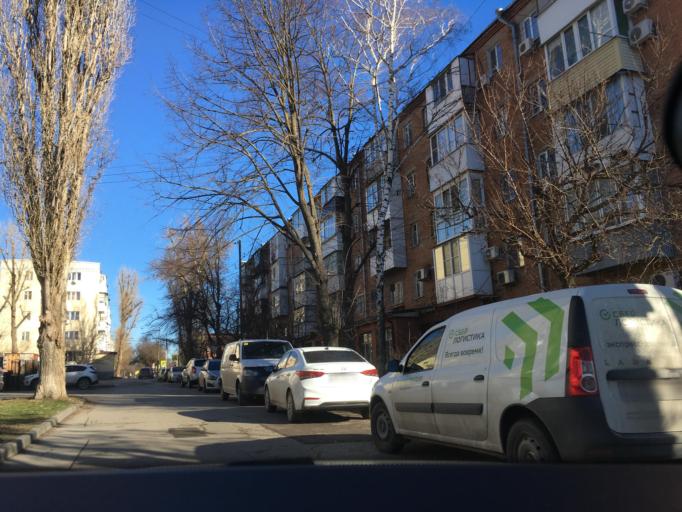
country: RU
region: Rostov
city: Imeni Chkalova
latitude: 47.2668
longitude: 39.7894
